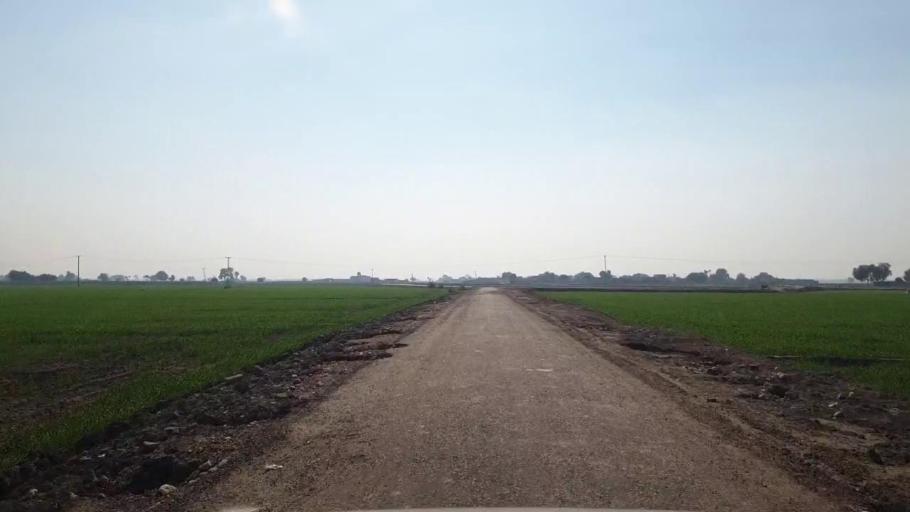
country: PK
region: Sindh
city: Bhan
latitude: 26.6509
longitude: 67.7018
